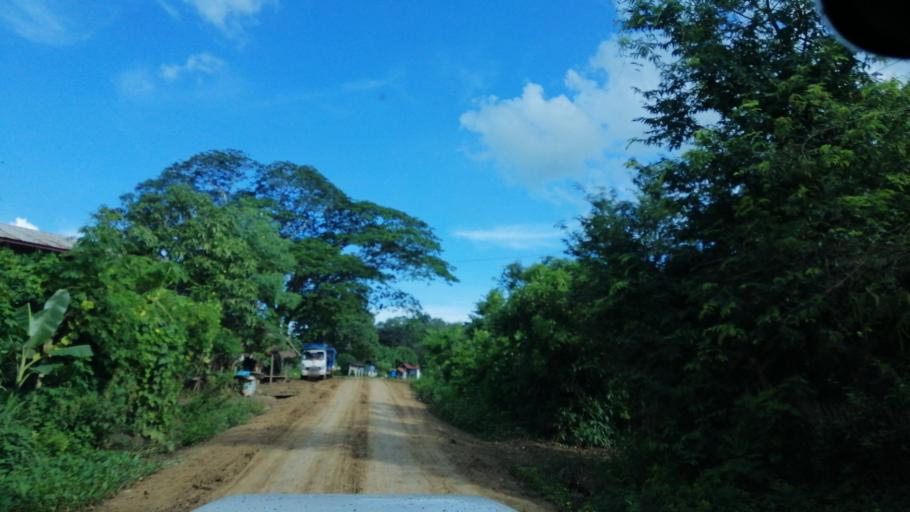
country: TH
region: Uttaradit
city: Ban Khok
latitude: 17.8732
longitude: 101.2195
